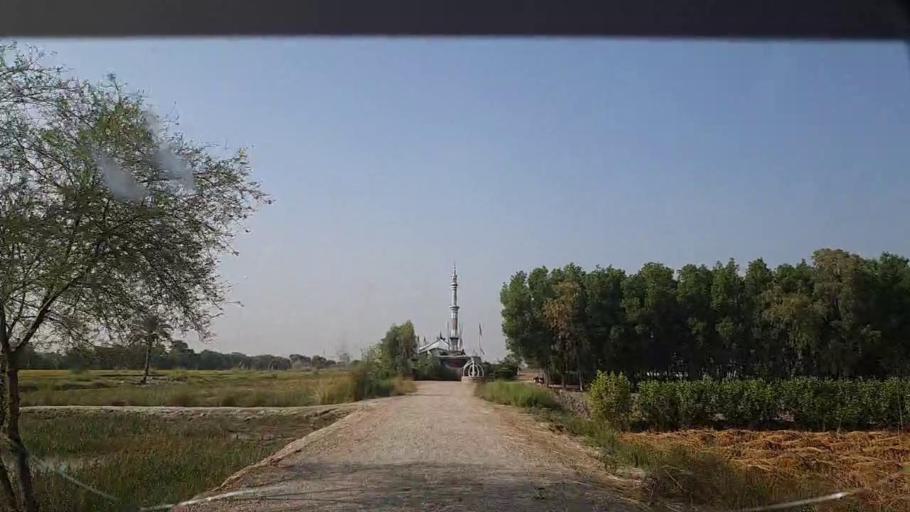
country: PK
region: Sindh
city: Shikarpur
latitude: 28.1203
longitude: 68.5717
